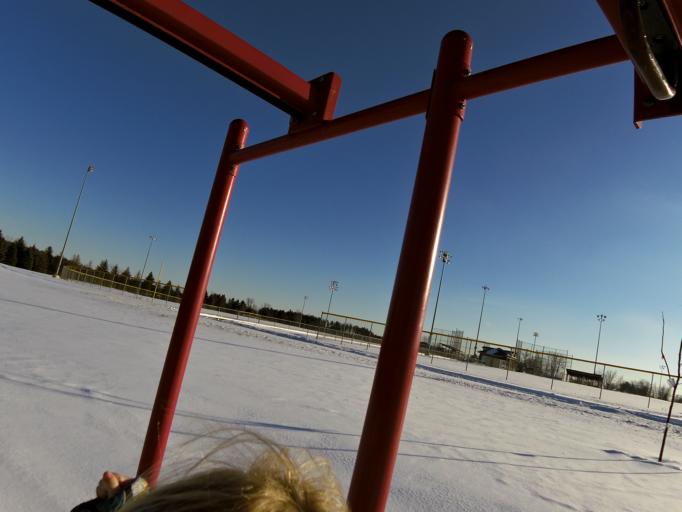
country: US
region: Wisconsin
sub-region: Saint Croix County
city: Hudson
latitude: 44.9803
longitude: -92.7180
